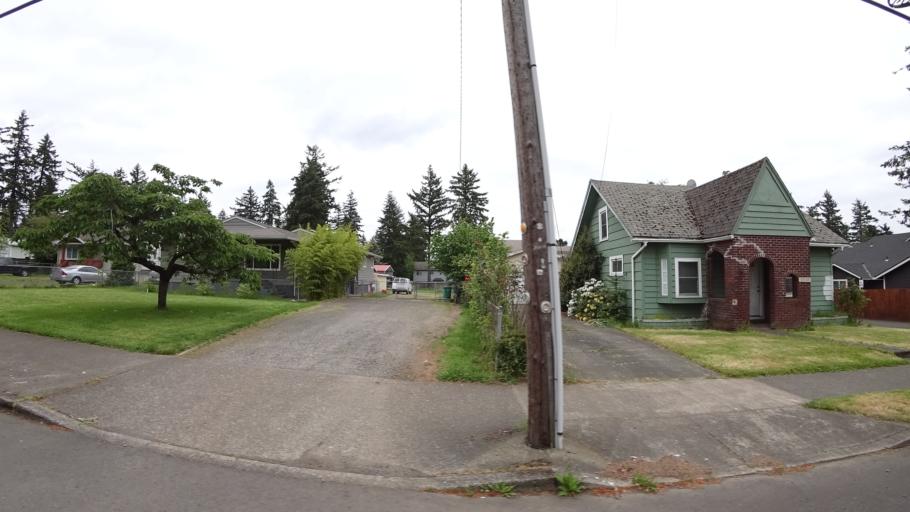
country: US
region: Oregon
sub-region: Multnomah County
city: Lents
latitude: 45.5067
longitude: -122.5299
